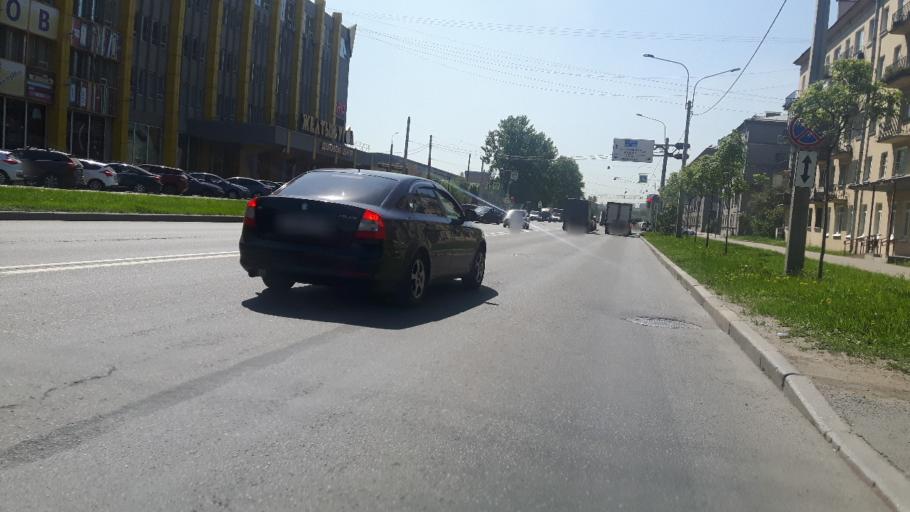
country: RU
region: St.-Petersburg
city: Admiralteisky
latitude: 59.8899
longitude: 30.2782
